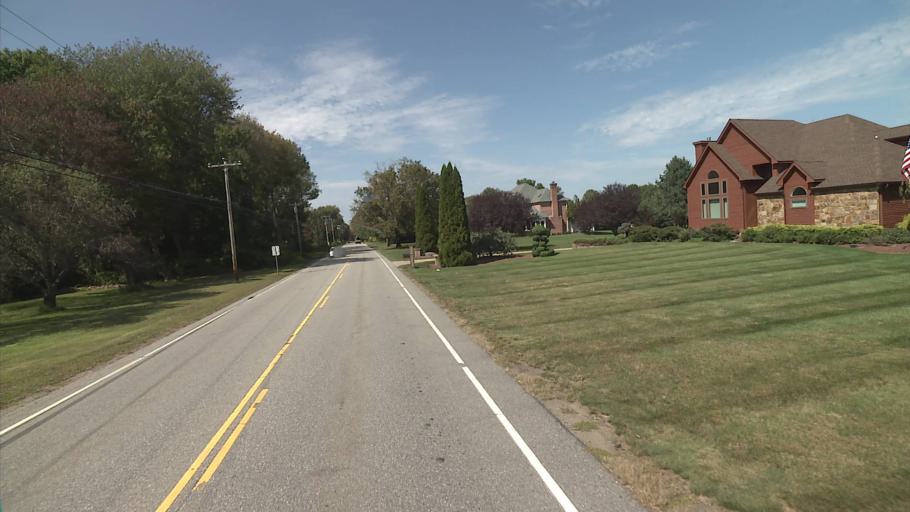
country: US
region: Connecticut
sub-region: Windham County
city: Willimantic
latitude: 41.6813
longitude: -72.2778
